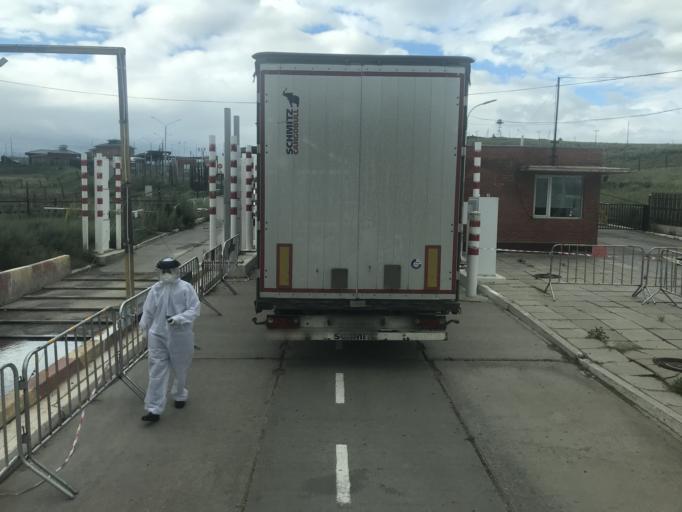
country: MN
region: Selenge
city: Altanbulag
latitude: 50.3230
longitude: 106.4895
